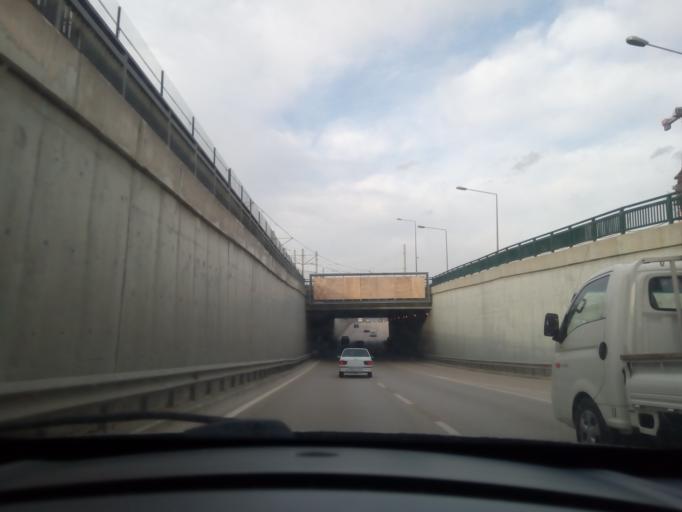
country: TR
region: Bursa
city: Cali
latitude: 40.2121
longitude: 28.9372
